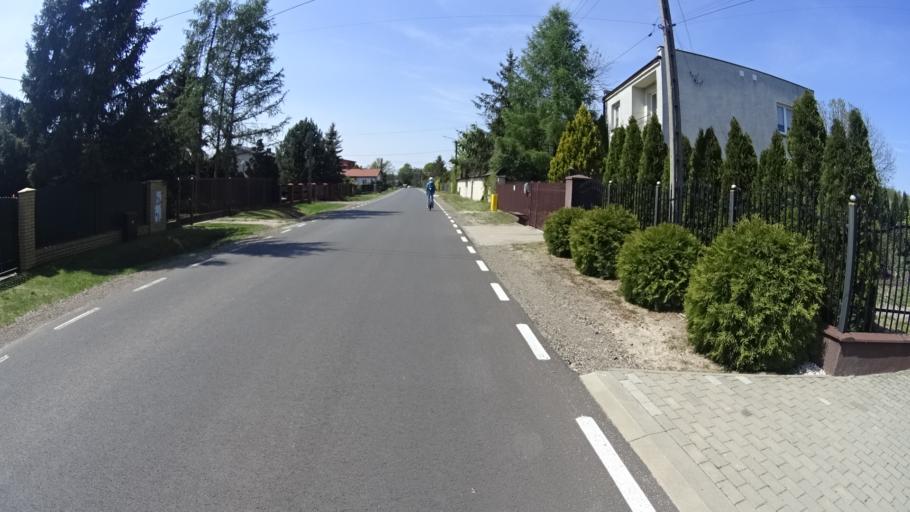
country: PL
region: Masovian Voivodeship
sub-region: Powiat warszawski zachodni
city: Truskaw
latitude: 52.2788
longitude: 20.7164
